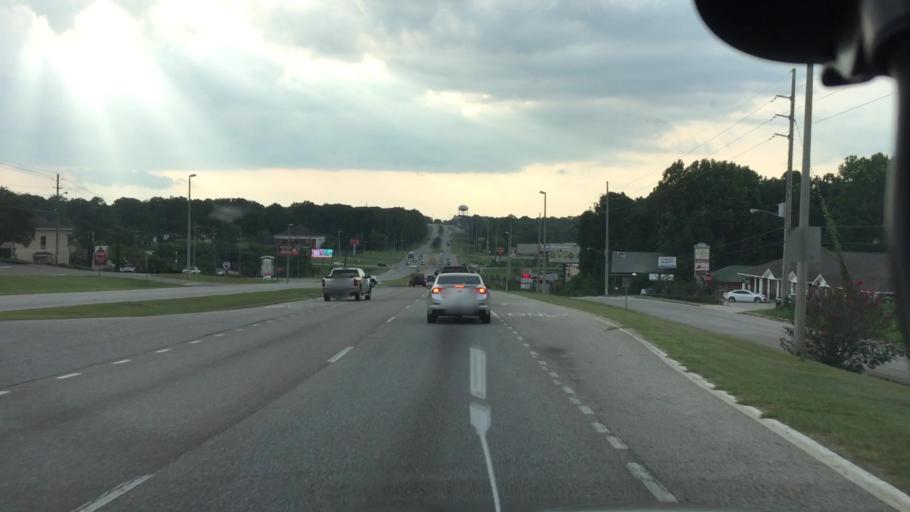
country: US
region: Alabama
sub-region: Coffee County
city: Enterprise
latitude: 31.3268
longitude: -85.8343
